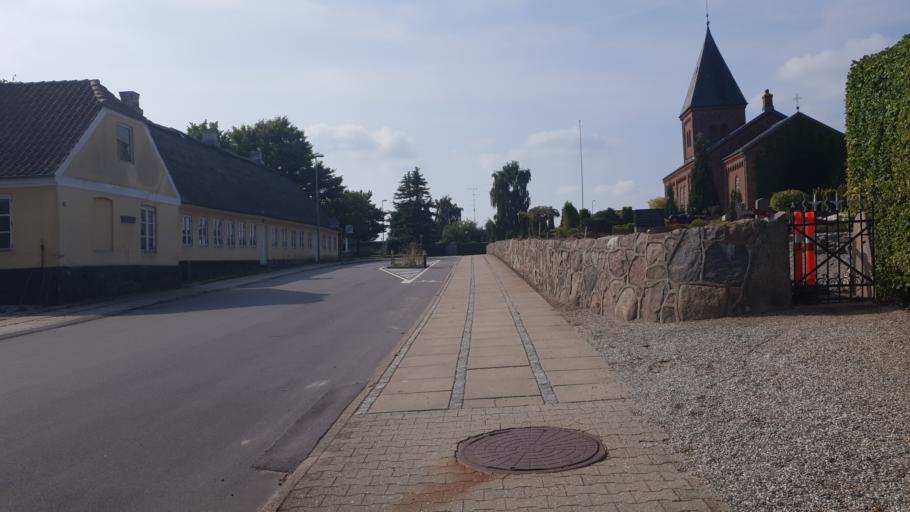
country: DK
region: South Denmark
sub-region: Fredericia Kommune
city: Snoghoj
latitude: 55.5476
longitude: 9.7013
